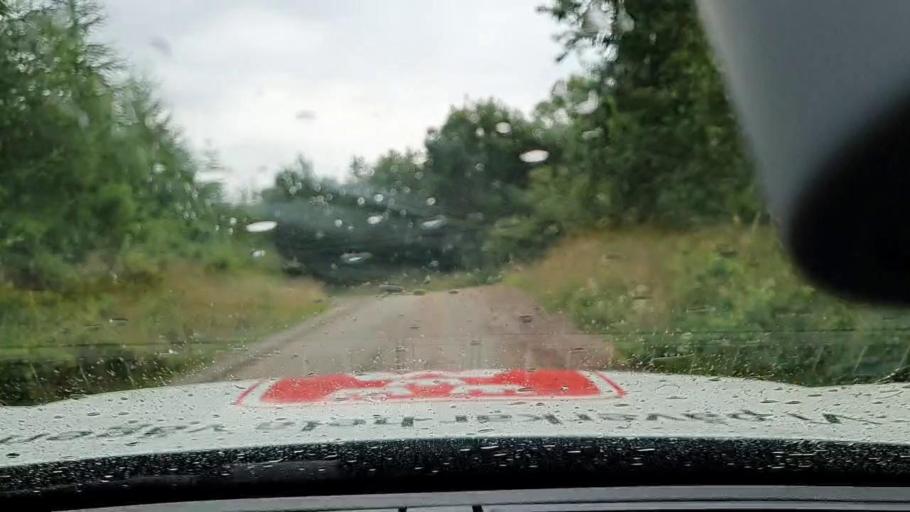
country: SE
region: Vaestra Goetaland
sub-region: Skara Kommun
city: Axvall
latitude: 58.4600
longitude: 13.6563
